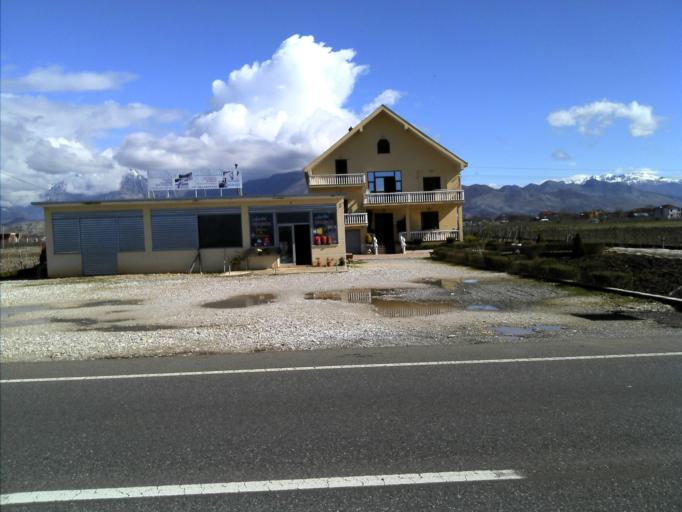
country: AL
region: Shkoder
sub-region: Rrethi i Malesia e Madhe
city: Grude-Fushe
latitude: 42.1460
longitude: 19.4802
